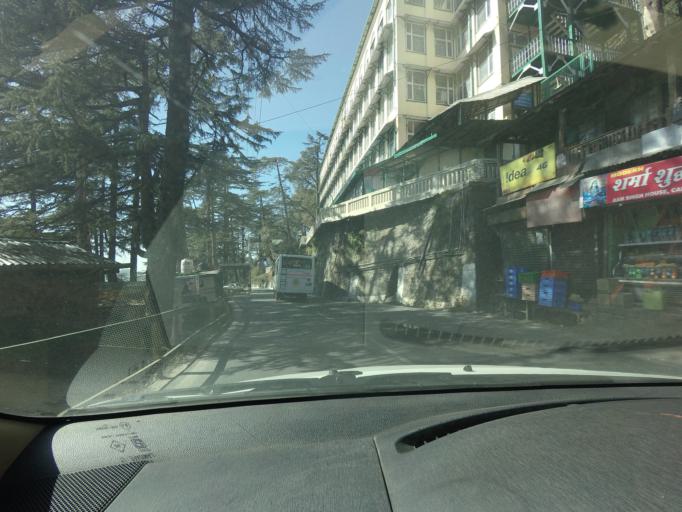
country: IN
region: Himachal Pradesh
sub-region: Shimla
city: Shimla
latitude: 31.1032
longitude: 77.1582
